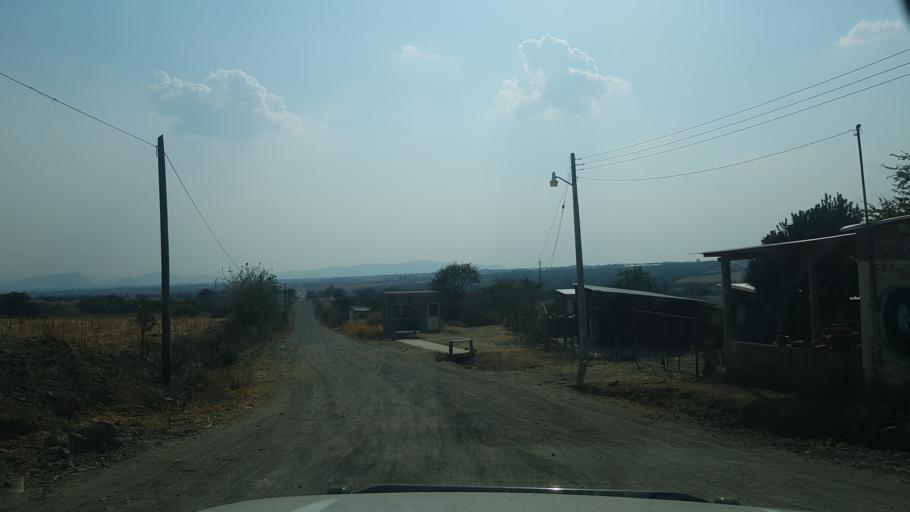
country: MX
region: Morelos
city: Tlacotepec
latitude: 18.7794
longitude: -98.7252
